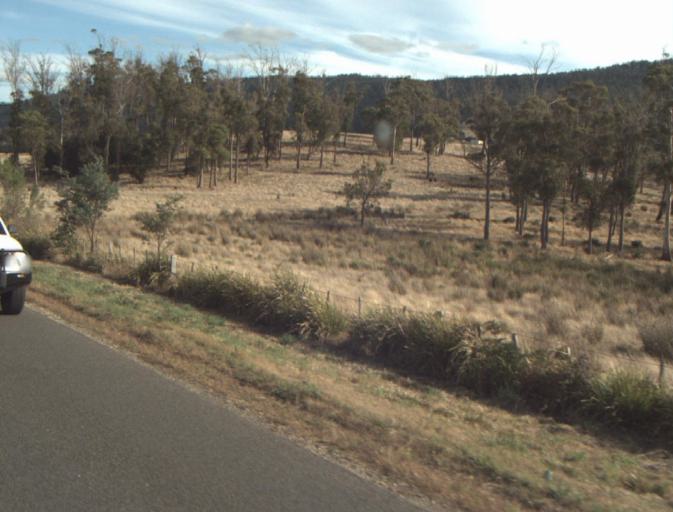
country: AU
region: Tasmania
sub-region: Launceston
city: Mayfield
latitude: -41.2159
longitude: 147.1214
